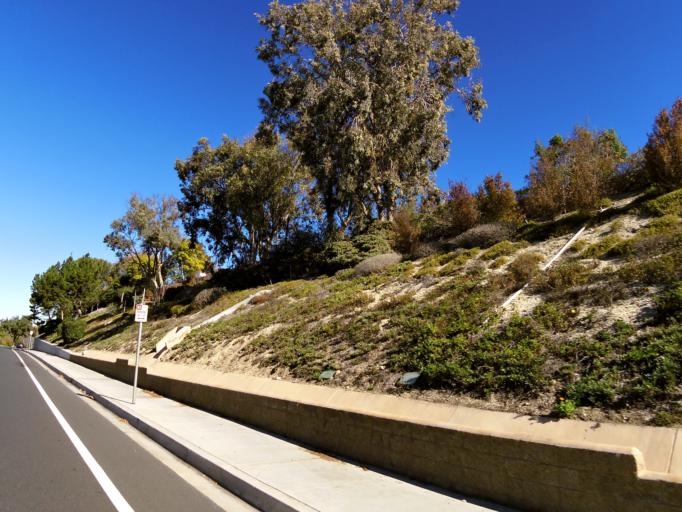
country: US
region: California
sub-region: Ventura County
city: Thousand Oaks
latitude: 34.1897
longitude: -118.8744
